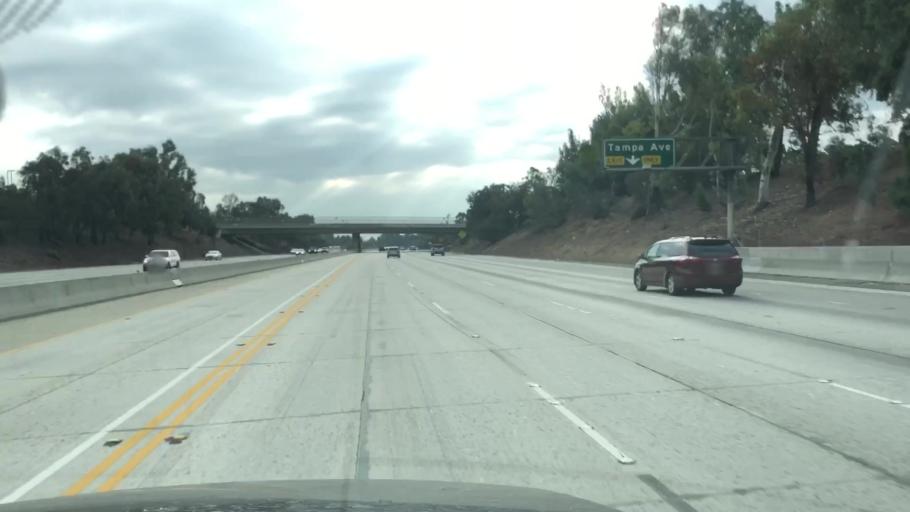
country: US
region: California
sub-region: Los Angeles County
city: Chatsworth
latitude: 34.2731
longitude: -118.5647
